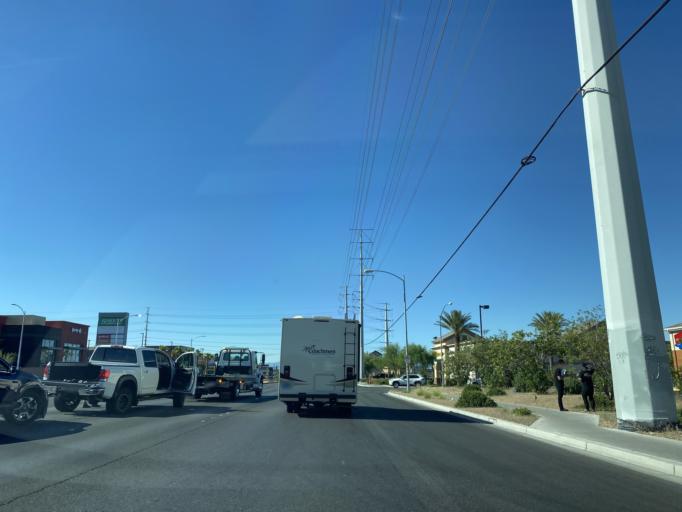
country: US
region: Nevada
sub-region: Clark County
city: Enterprise
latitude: 36.0534
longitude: -115.2430
